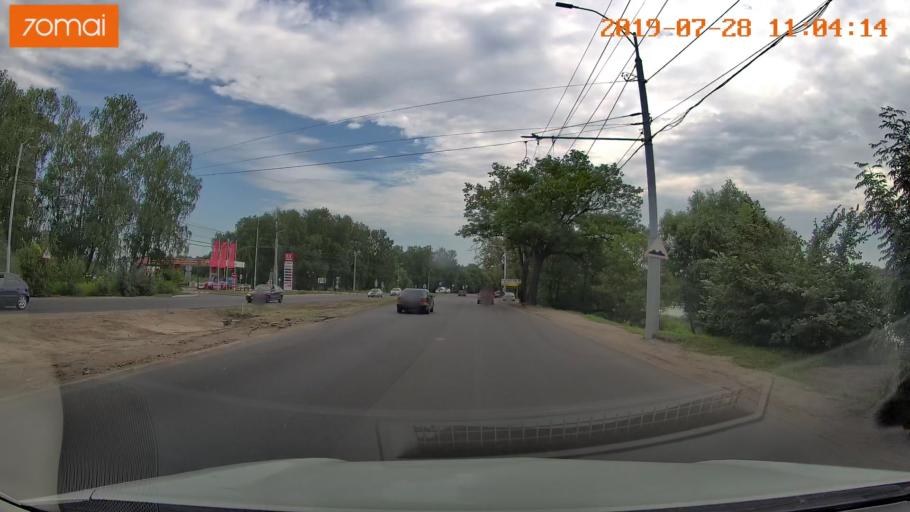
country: RU
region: Kaliningrad
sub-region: Gorod Kaliningrad
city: Kaliningrad
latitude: 54.7156
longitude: 20.3771
